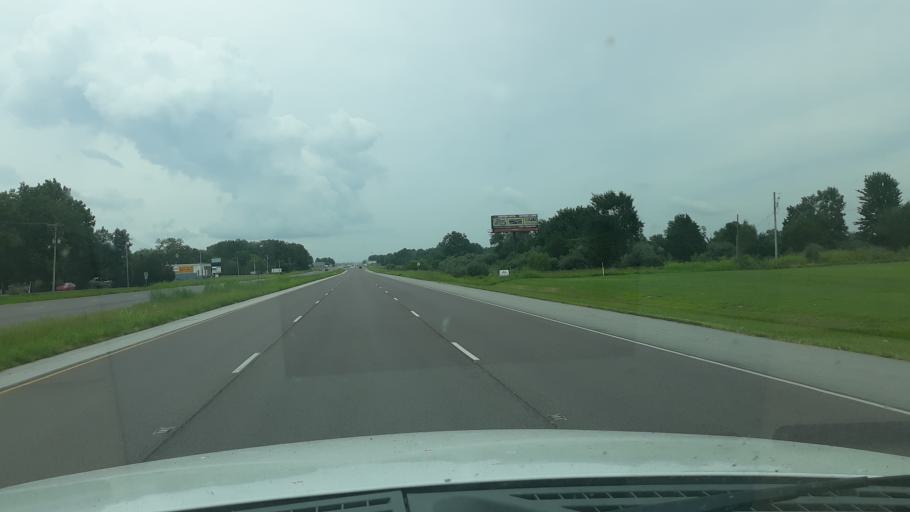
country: US
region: Illinois
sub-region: Williamson County
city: Crainville
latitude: 37.7450
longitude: -89.0440
